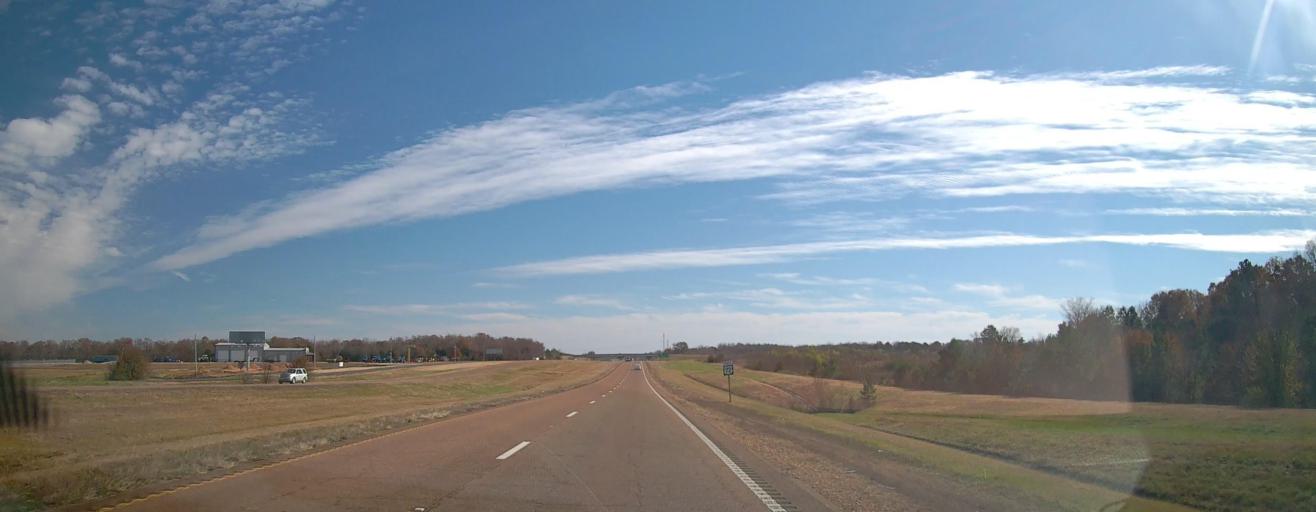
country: US
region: Tennessee
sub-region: Fayette County
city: Piperton
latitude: 34.9693
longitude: -89.5537
